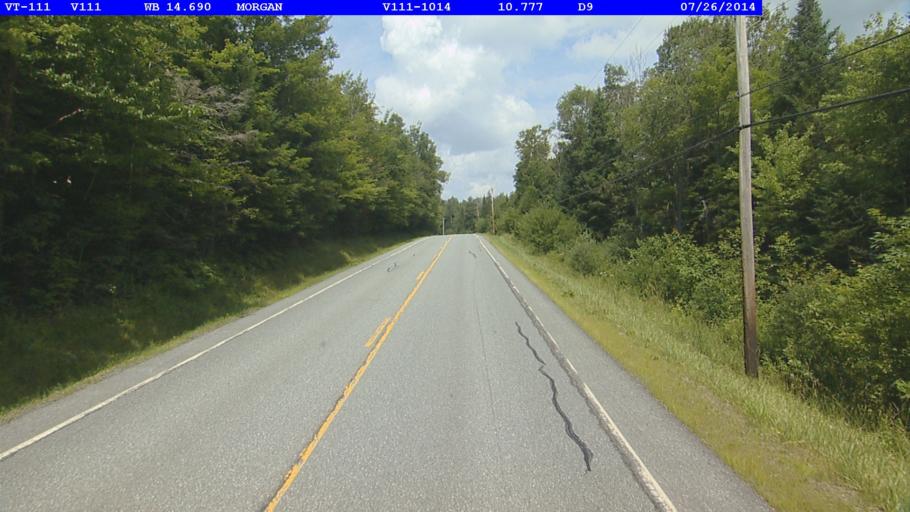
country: US
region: Vermont
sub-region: Orleans County
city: Newport
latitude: 44.8500
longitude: -71.9138
